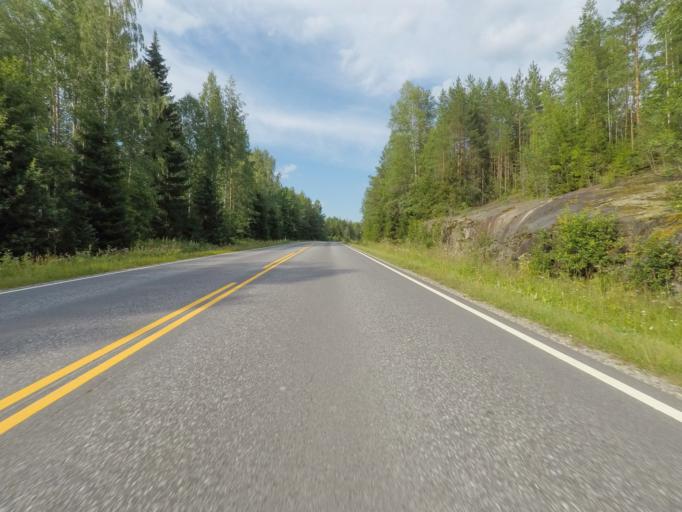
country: FI
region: Southern Savonia
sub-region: Savonlinna
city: Sulkava
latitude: 61.8960
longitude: 28.5777
